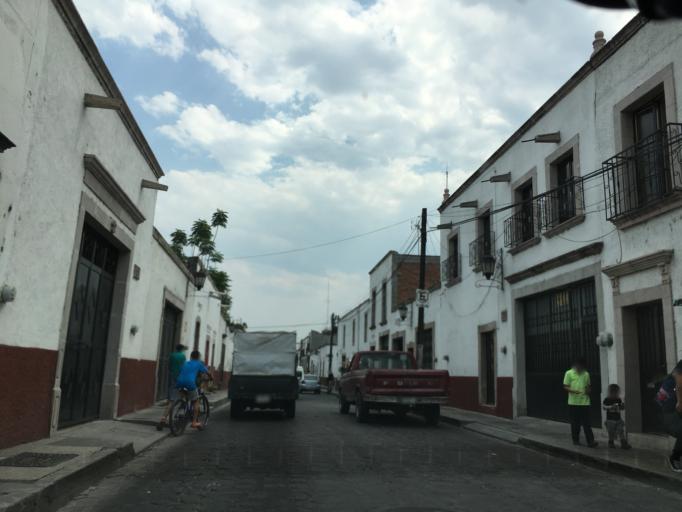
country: MX
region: Michoacan
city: Cuitzeo del Porvenir
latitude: 19.9707
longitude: -101.1403
